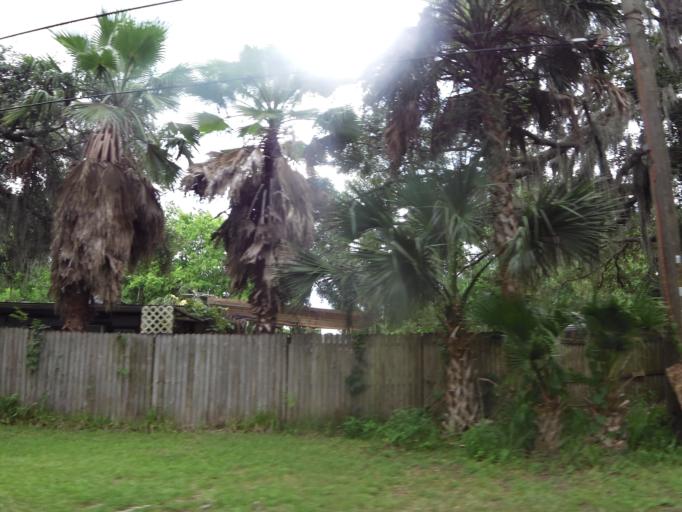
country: US
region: Florida
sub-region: Duval County
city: Atlantic Beach
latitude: 30.3327
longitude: -81.4258
